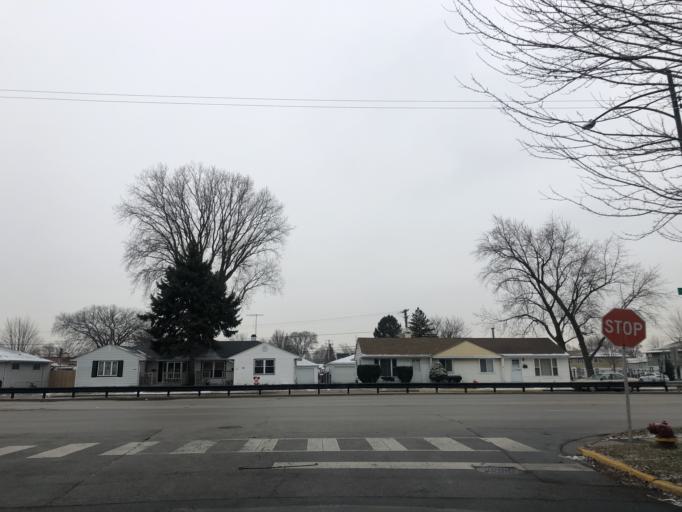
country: US
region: Illinois
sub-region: Cook County
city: Hometown
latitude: 41.7349
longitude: -87.7361
